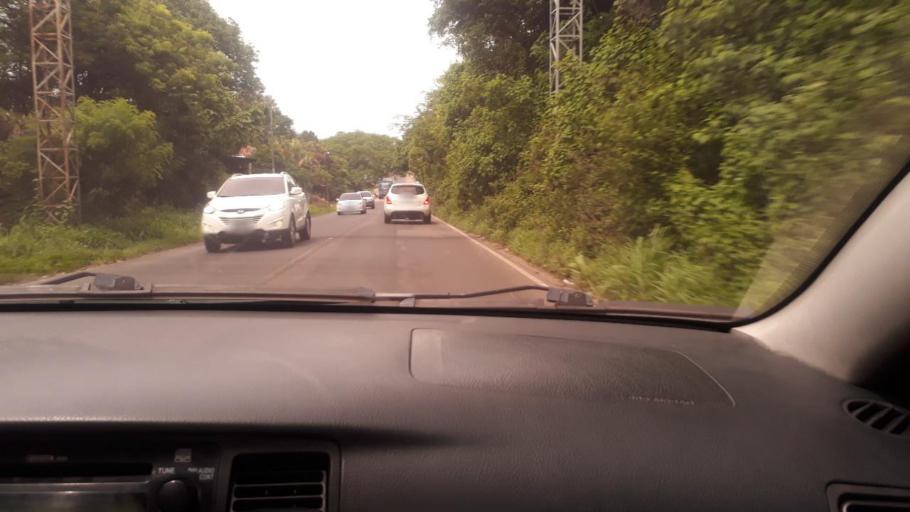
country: GT
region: Jutiapa
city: Jutiapa
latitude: 14.2835
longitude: -89.9507
